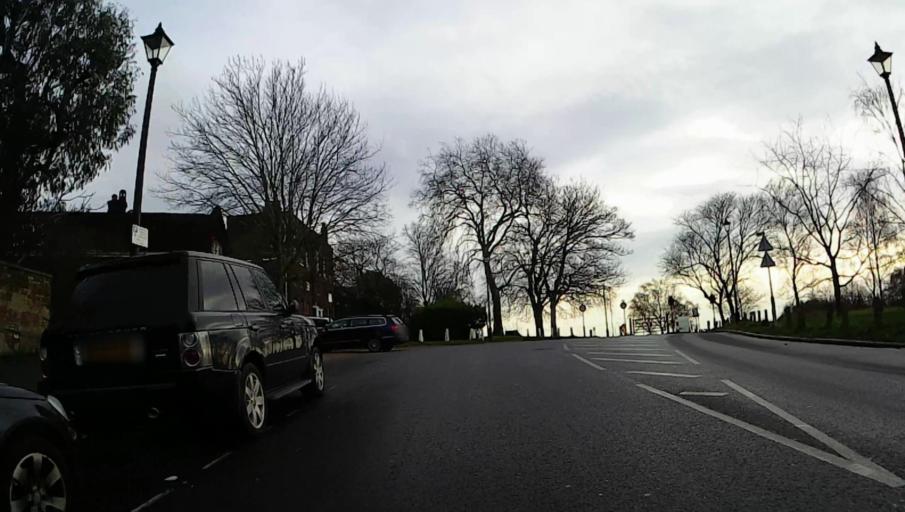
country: GB
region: England
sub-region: Greater London
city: Blackheath
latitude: 51.4752
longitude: -0.0041
